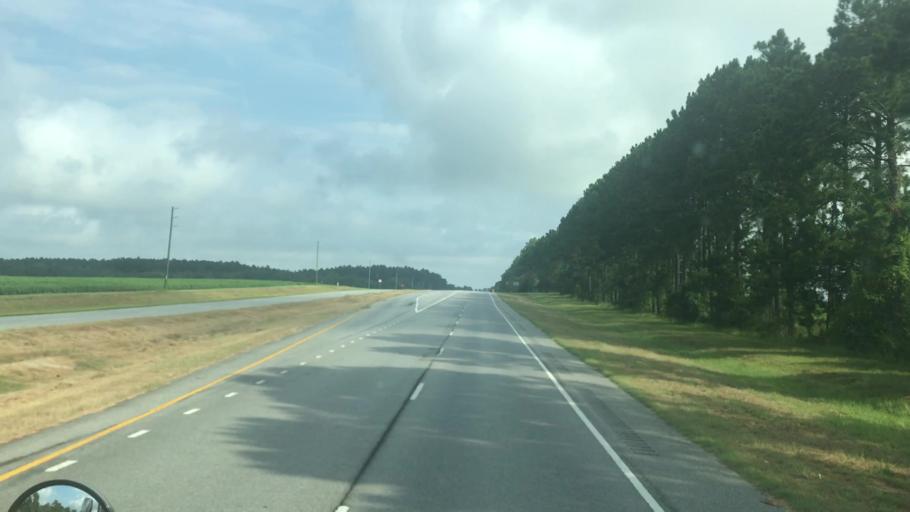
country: US
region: Georgia
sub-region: Miller County
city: Colquitt
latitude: 31.1903
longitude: -84.7647
